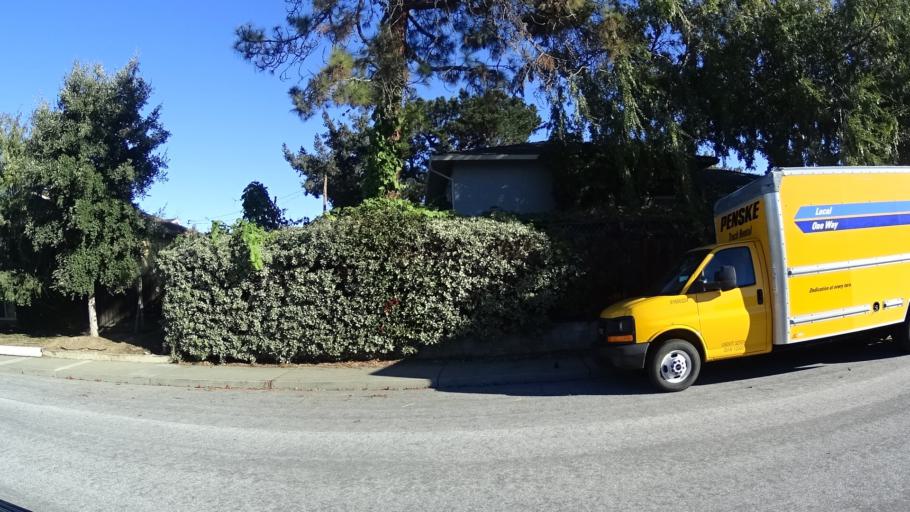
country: US
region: California
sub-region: Santa Clara County
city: Cupertino
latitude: 37.3409
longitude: -122.0294
